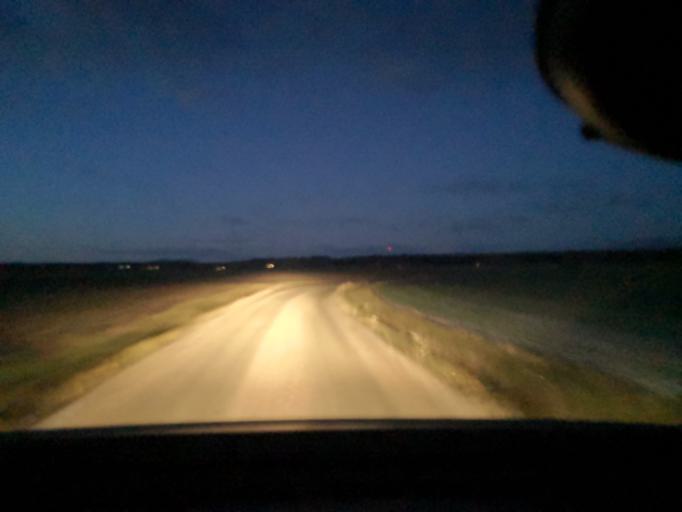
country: SE
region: Uppsala
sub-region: Heby Kommun
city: Heby
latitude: 59.9212
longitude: 16.7509
